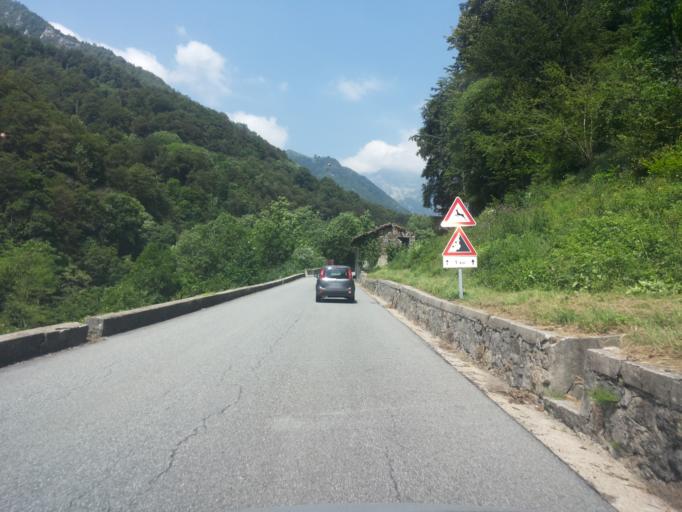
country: IT
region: Piedmont
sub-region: Provincia di Biella
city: Campiglia Cervo
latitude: 45.6655
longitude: 7.9952
